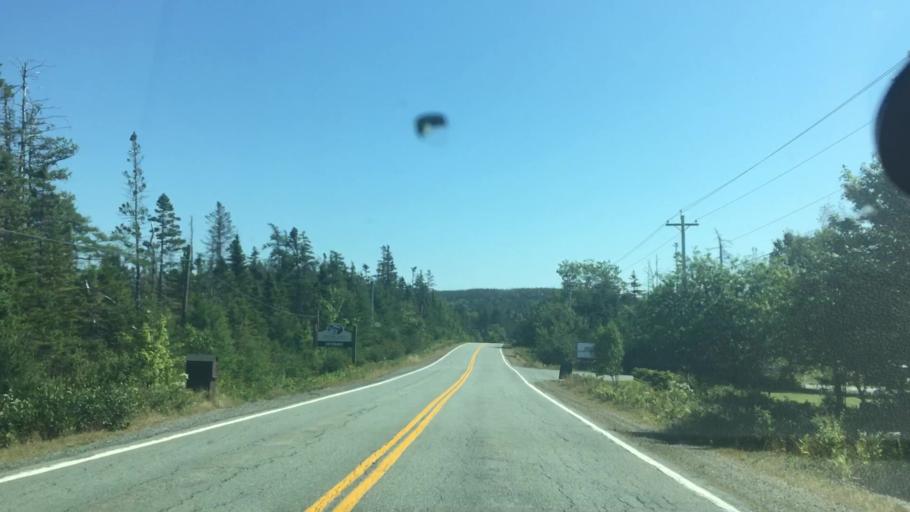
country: CA
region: Nova Scotia
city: Antigonish
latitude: 45.0135
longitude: -62.1019
